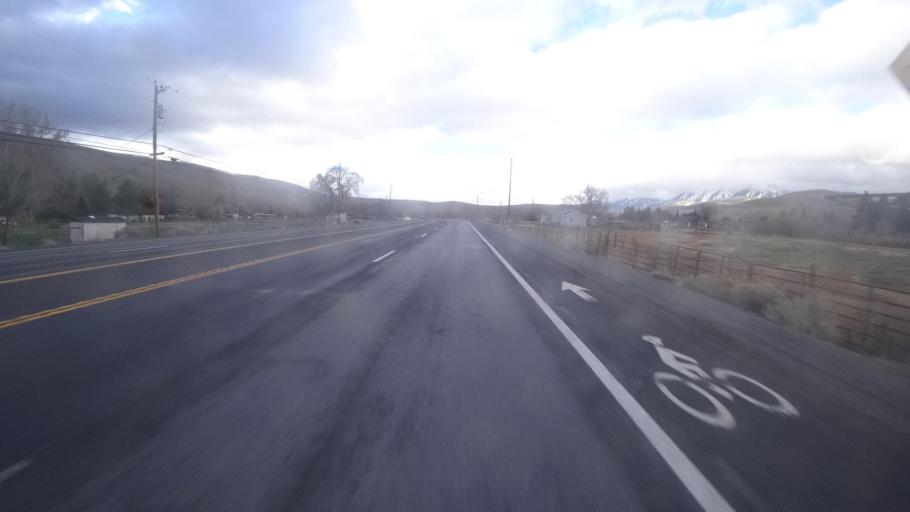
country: US
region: Nevada
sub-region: Storey County
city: Virginia City
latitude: 39.3501
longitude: -119.7780
